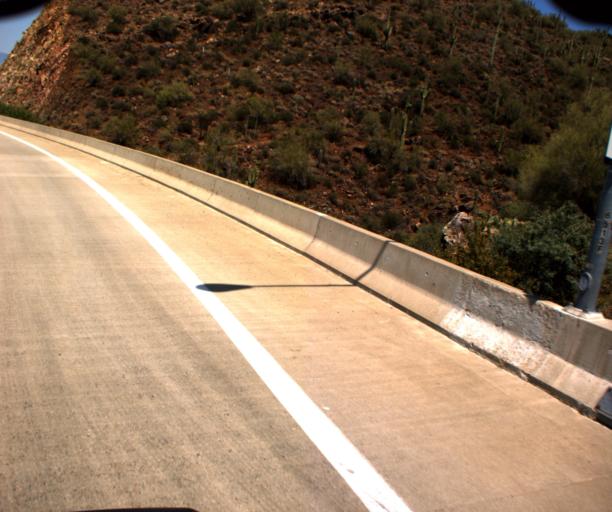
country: US
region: Arizona
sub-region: Gila County
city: Tonto Basin
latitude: 33.6726
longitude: -111.1530
